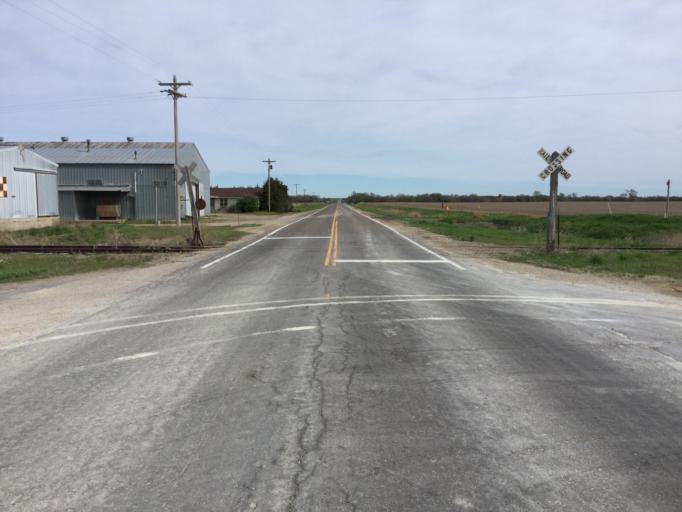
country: US
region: Kansas
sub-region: Osborne County
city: Osborne
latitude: 39.4158
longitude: -98.5455
